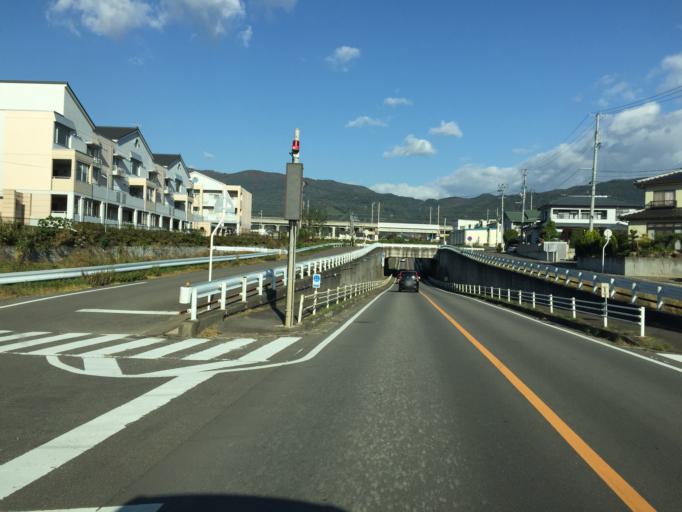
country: JP
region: Fukushima
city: Hobaramachi
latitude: 37.8760
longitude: 140.5377
